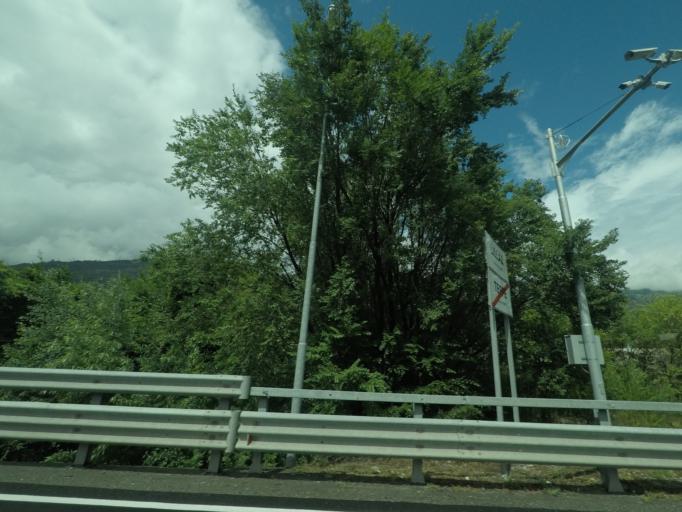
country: IT
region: Aosta Valley
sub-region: Valle d'Aosta
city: Villair-Amerique
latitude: 45.7411
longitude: 7.3905
